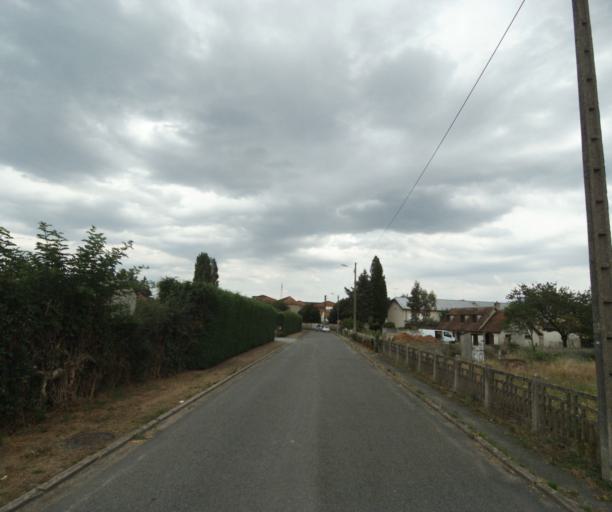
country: FR
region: Bourgogne
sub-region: Departement de Saone-et-Loire
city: Gueugnon
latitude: 46.6076
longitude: 4.0604
